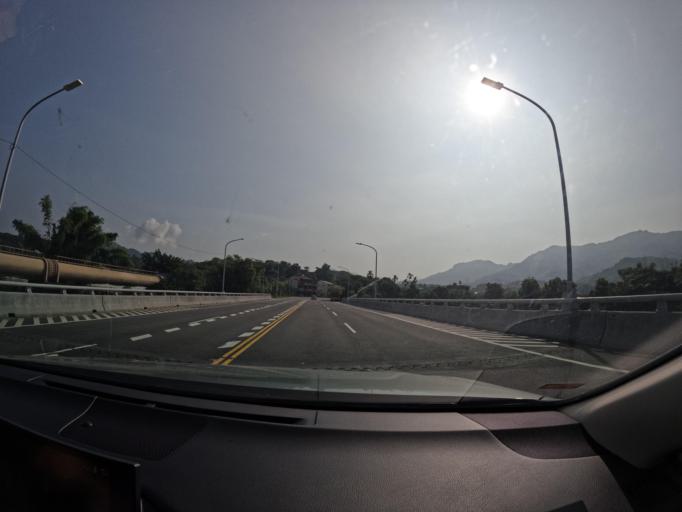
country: TW
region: Taiwan
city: Yujing
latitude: 23.0746
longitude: 120.4972
